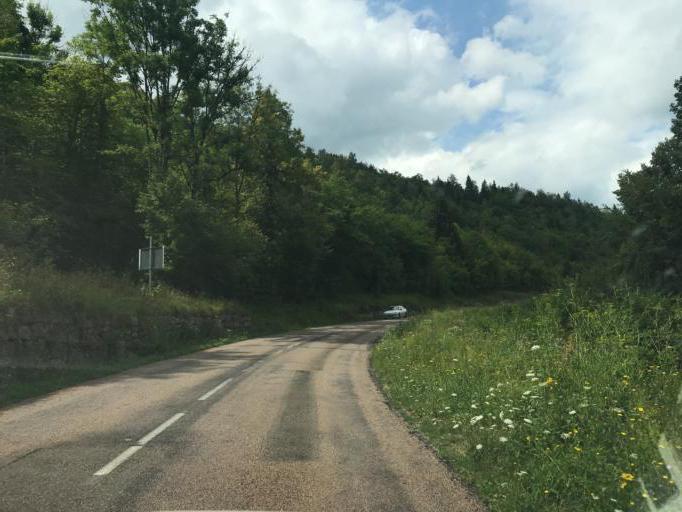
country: FR
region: Franche-Comte
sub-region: Departement du Jura
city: Valfin-les-Saint-Claude
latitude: 46.4304
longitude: 5.8568
